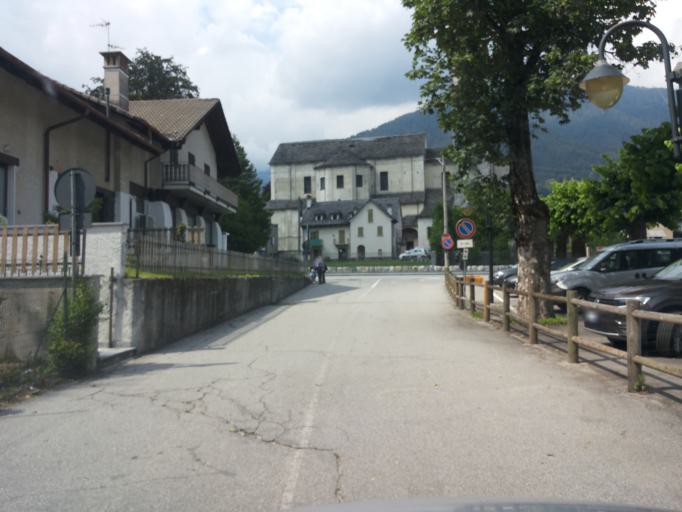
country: IT
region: Piedmont
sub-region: Provincia Verbano-Cusio-Ossola
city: Santa Maria Maggiore
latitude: 46.1336
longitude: 8.4668
